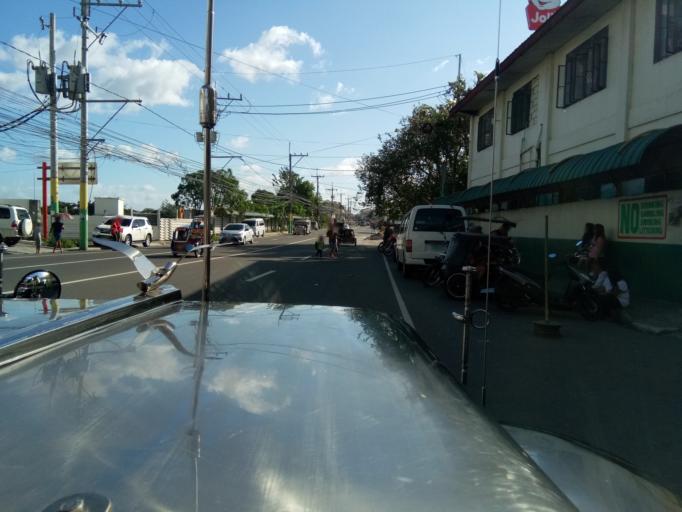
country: PH
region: Calabarzon
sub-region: Province of Cavite
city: Dasmarinas
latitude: 14.3533
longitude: 120.9812
